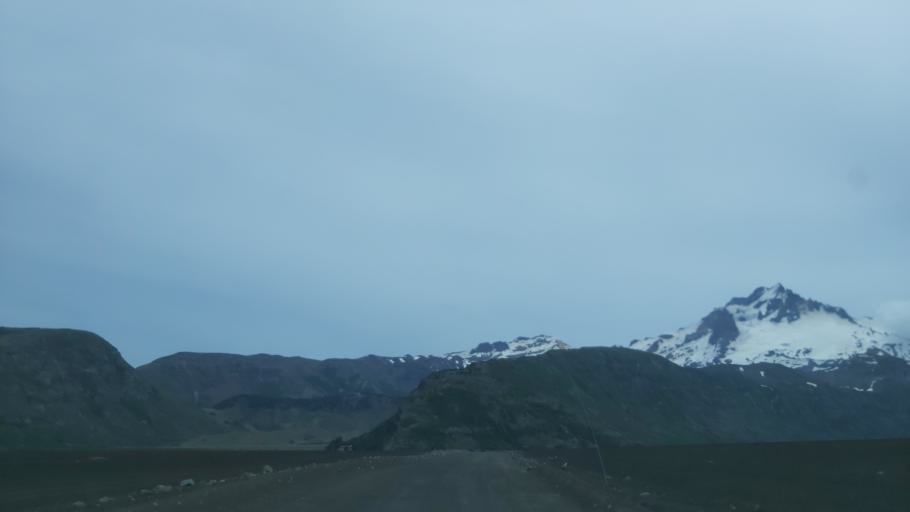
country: AR
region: Neuquen
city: Andacollo
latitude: -37.4595
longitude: -71.3047
